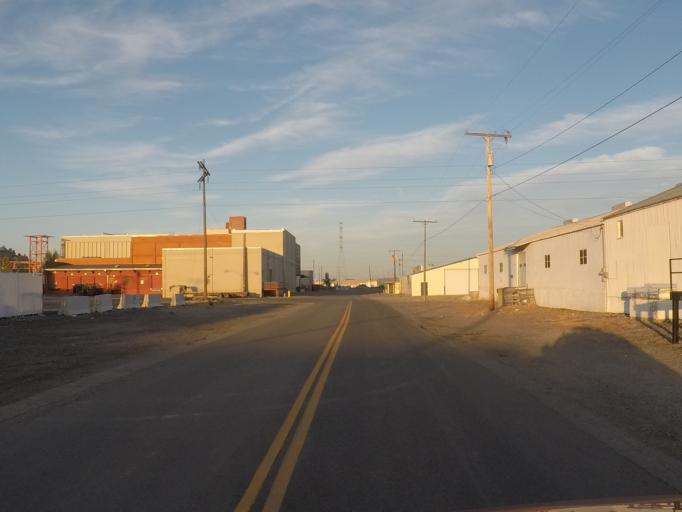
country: US
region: Montana
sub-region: Yellowstone County
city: Billings
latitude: 45.7885
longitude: -108.4898
